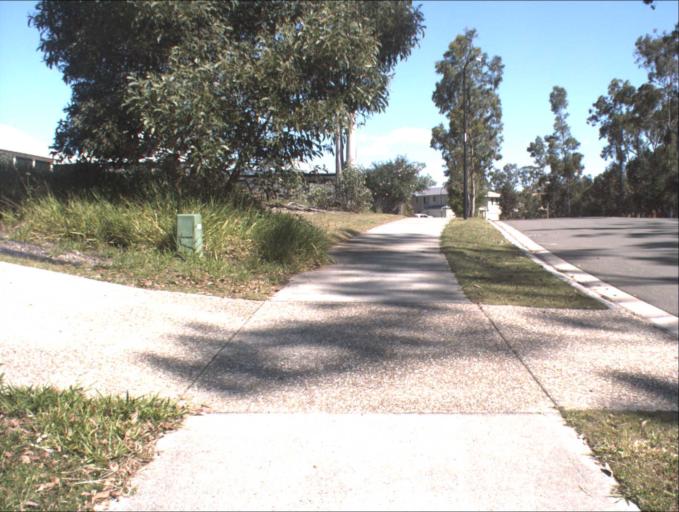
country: AU
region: Queensland
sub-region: Logan
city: Waterford West
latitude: -27.7171
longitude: 153.1530
